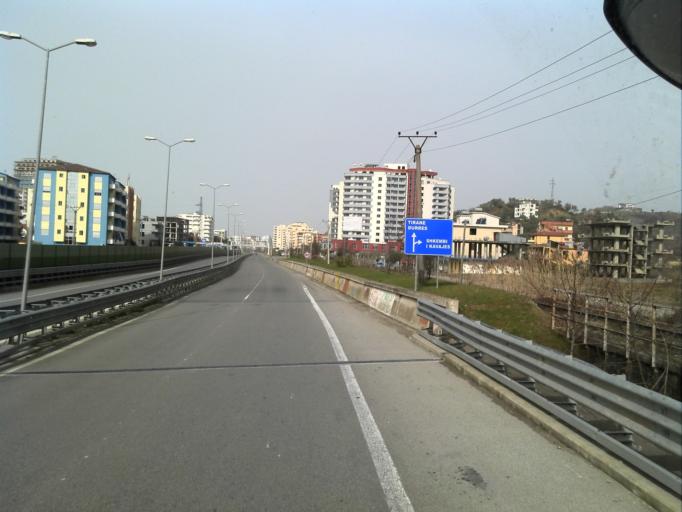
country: AL
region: Tirane
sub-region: Rrethi i Kavajes
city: Golem
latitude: 41.2648
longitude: 19.5239
